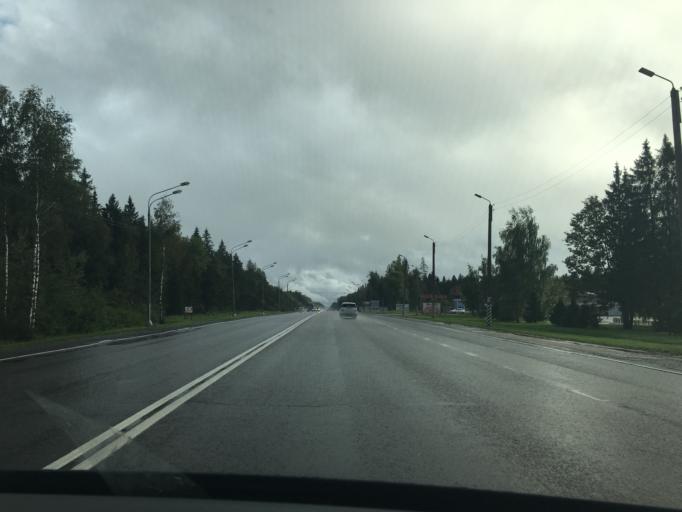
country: RU
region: Kaluga
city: Balabanovo
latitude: 55.1647
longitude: 36.6689
